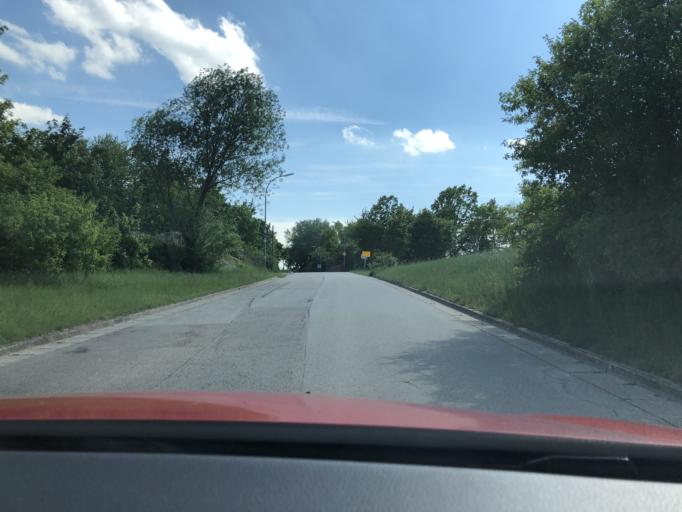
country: DE
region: Bavaria
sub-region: Upper Bavaria
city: Lenting
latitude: 48.7769
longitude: 11.4872
